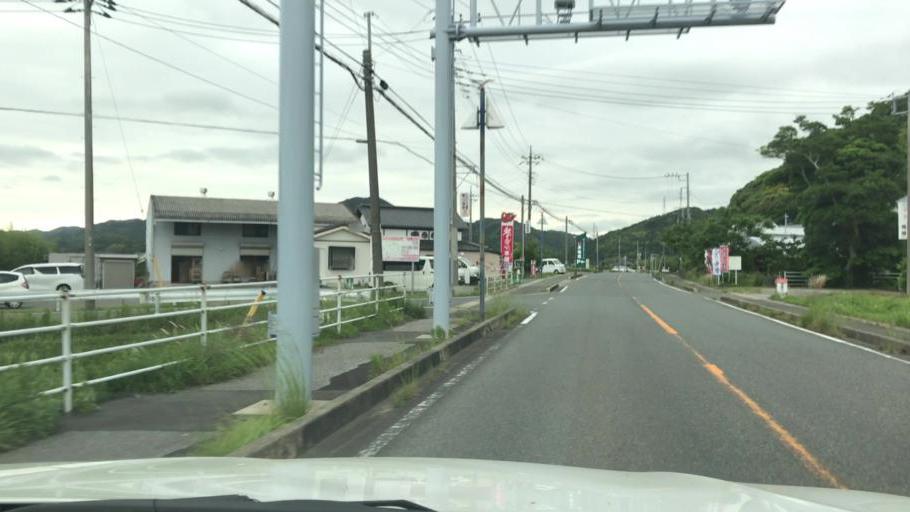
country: JP
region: Chiba
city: Kawaguchi
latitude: 35.1247
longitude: 140.0808
